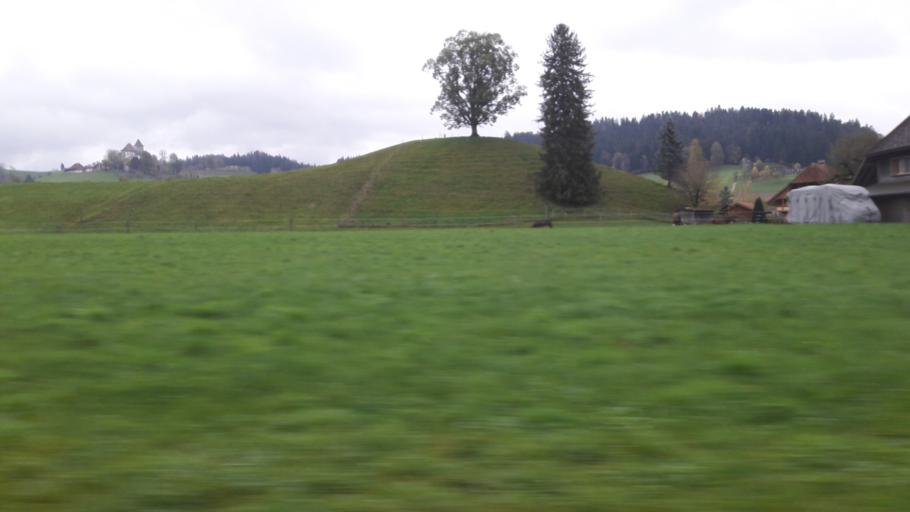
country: CH
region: Bern
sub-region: Emmental District
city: Trachselwald
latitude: 47.0164
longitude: 7.7271
